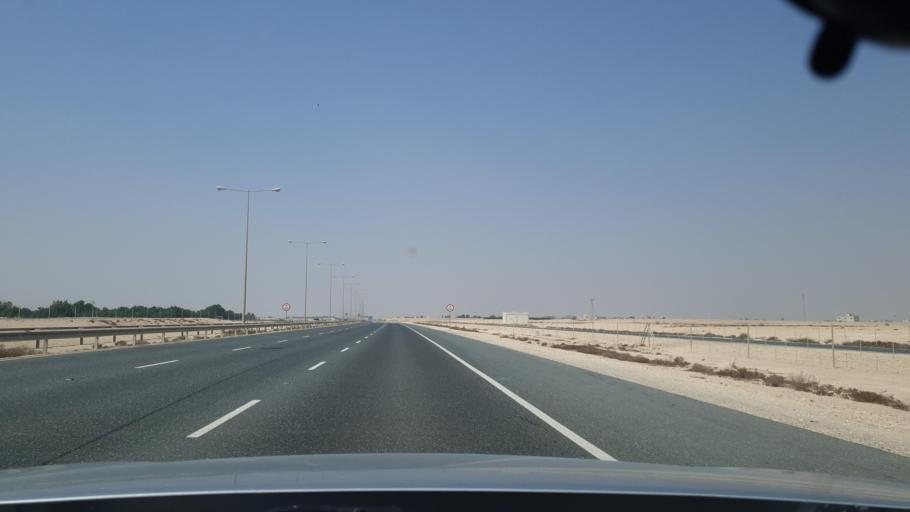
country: QA
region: Al Khawr
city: Al Khawr
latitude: 25.7739
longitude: 51.4110
